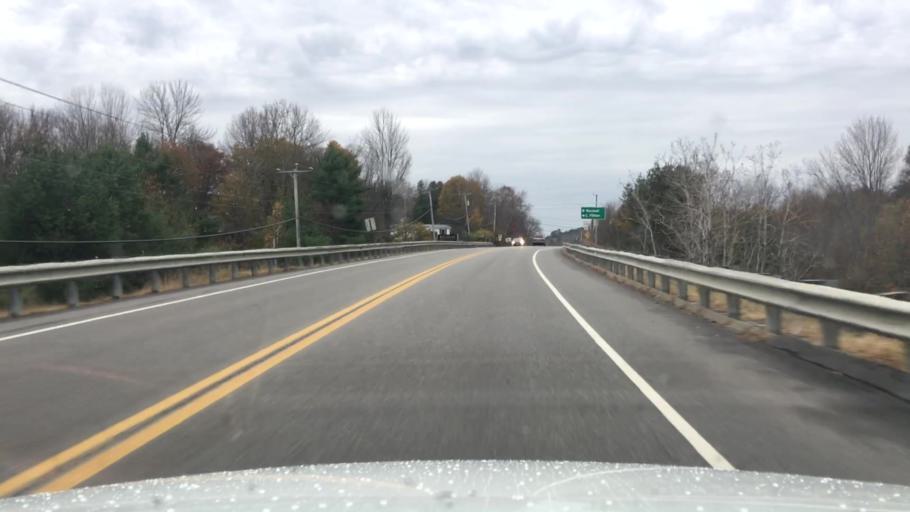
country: US
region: Maine
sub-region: Kennebec County
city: Pittston
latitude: 44.2188
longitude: -69.7561
